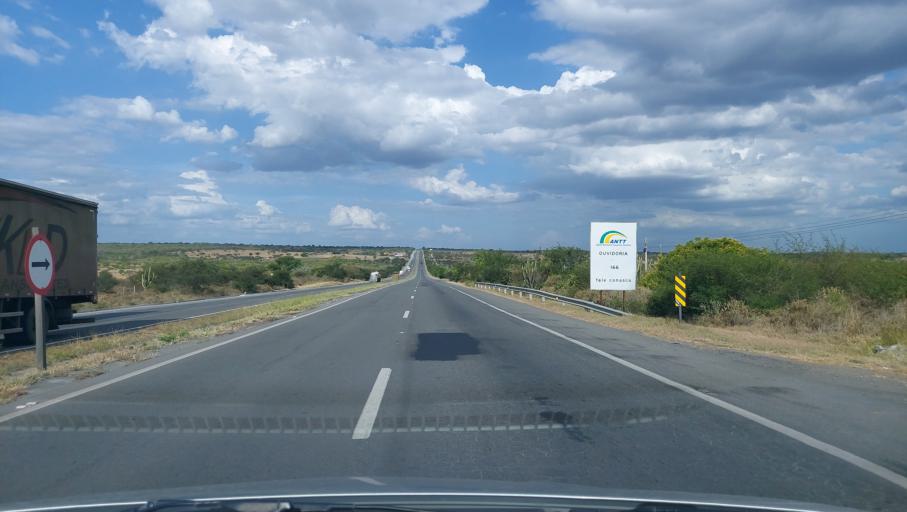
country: BR
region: Bahia
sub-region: Castro Alves
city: Castro Alves
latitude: -12.5747
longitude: -39.5028
